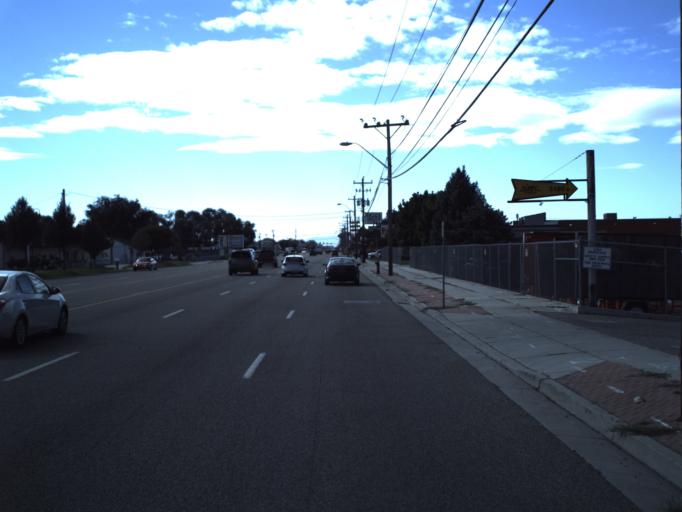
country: US
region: Utah
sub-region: Salt Lake County
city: Taylorsville
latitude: 40.7027
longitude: -111.9391
